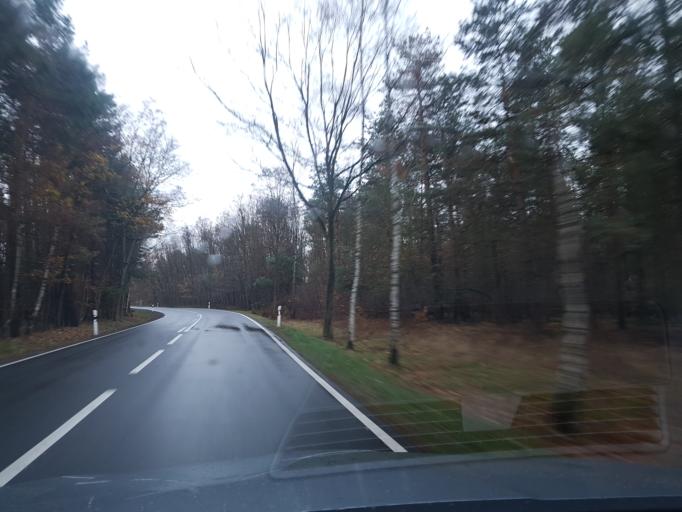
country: DE
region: Brandenburg
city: Finsterwalde
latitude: 51.6522
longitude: 13.6927
